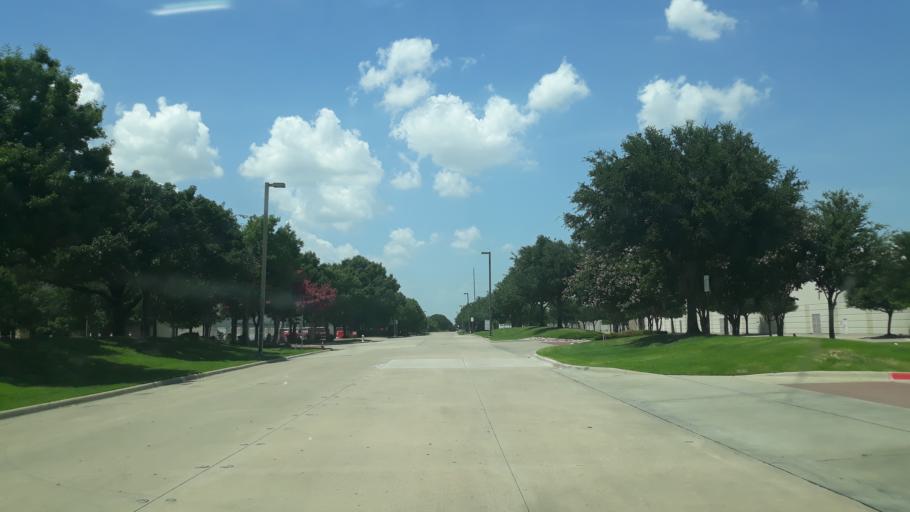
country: US
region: Texas
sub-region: Dallas County
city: Coppell
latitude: 32.9696
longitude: -97.0199
